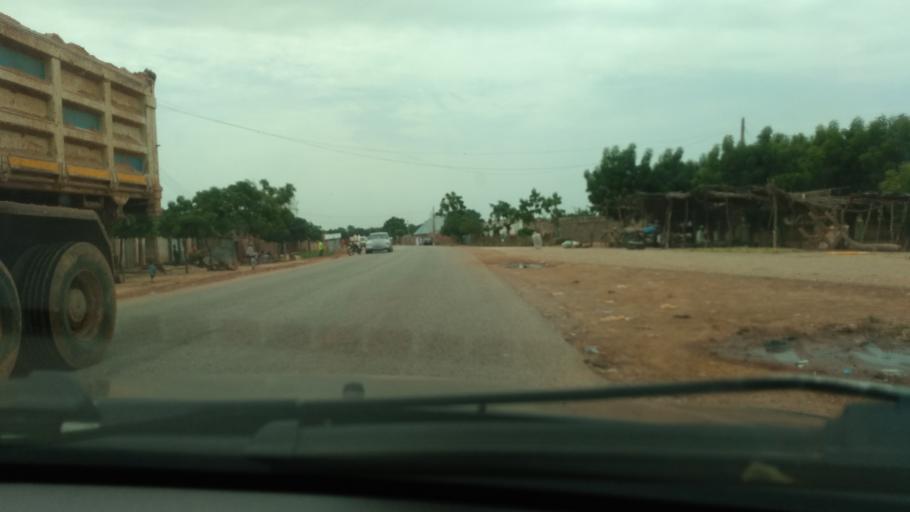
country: NG
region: Katsina
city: Kankia
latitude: 12.4056
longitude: 7.7204
